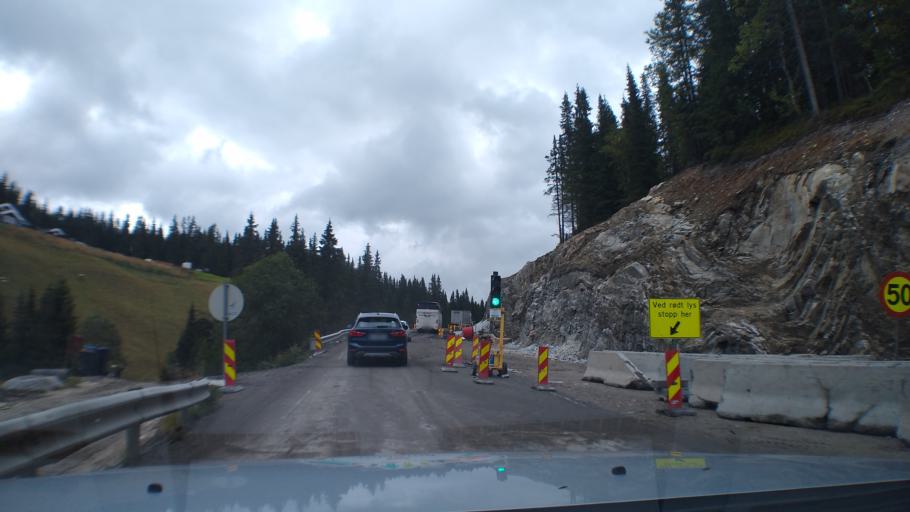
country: NO
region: Oppland
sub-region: Ringebu
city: Ringebu
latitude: 61.5986
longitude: 10.0548
